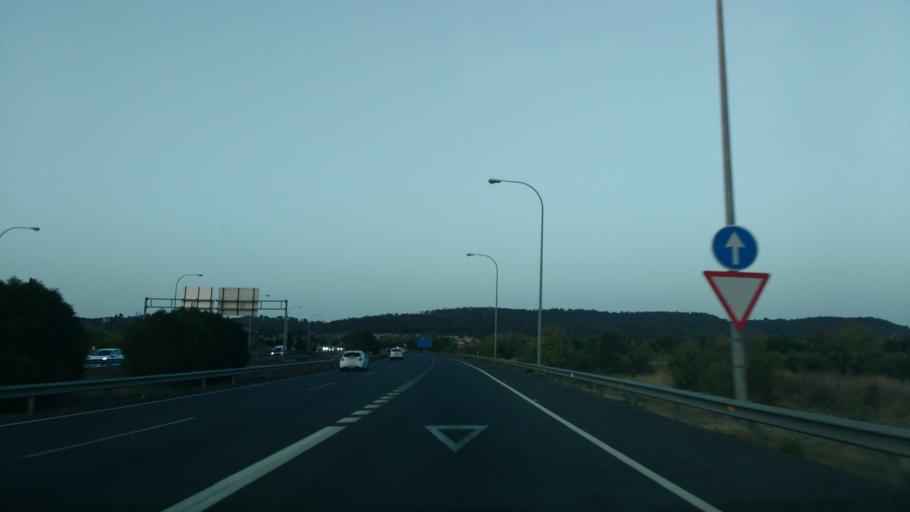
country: ES
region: Balearic Islands
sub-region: Illes Balears
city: Marratxi
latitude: 39.6304
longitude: 2.7409
